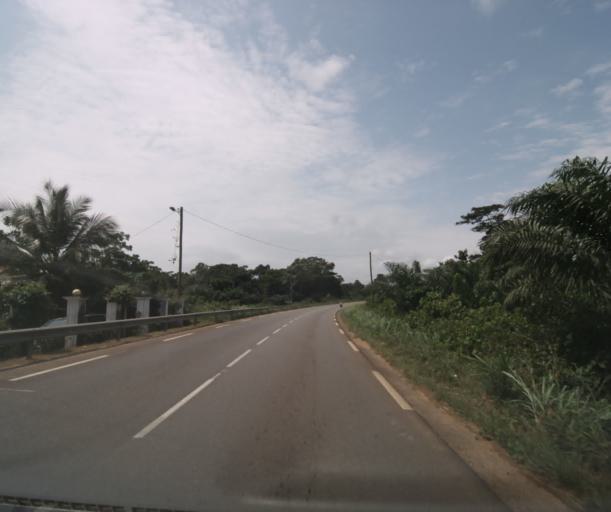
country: CM
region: South Province
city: Kribi
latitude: 3.0190
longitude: 9.9574
